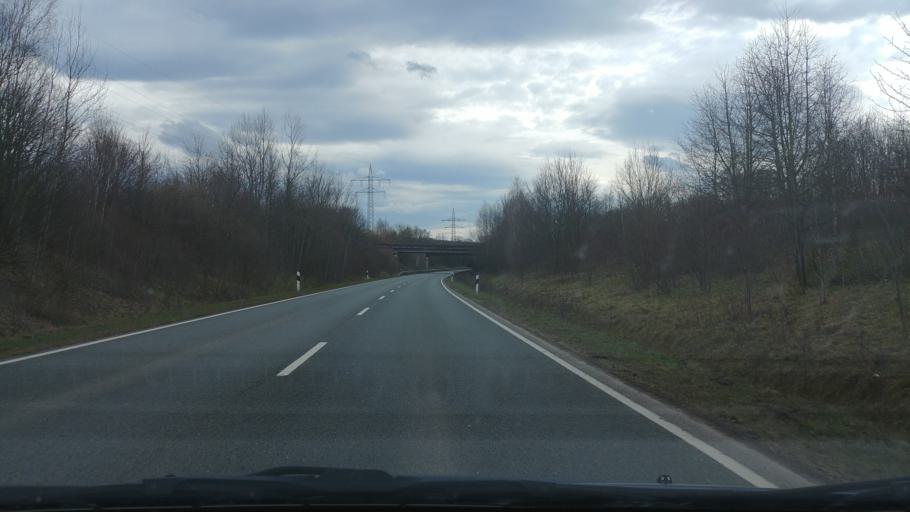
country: DE
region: Lower Saxony
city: Bevern
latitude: 51.8328
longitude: 9.4821
